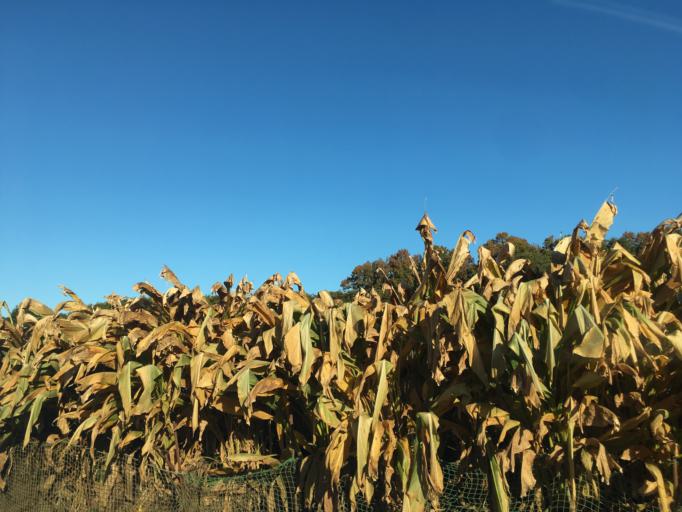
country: JP
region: Saitama
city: Tokorozawa
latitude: 35.8003
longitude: 139.4938
